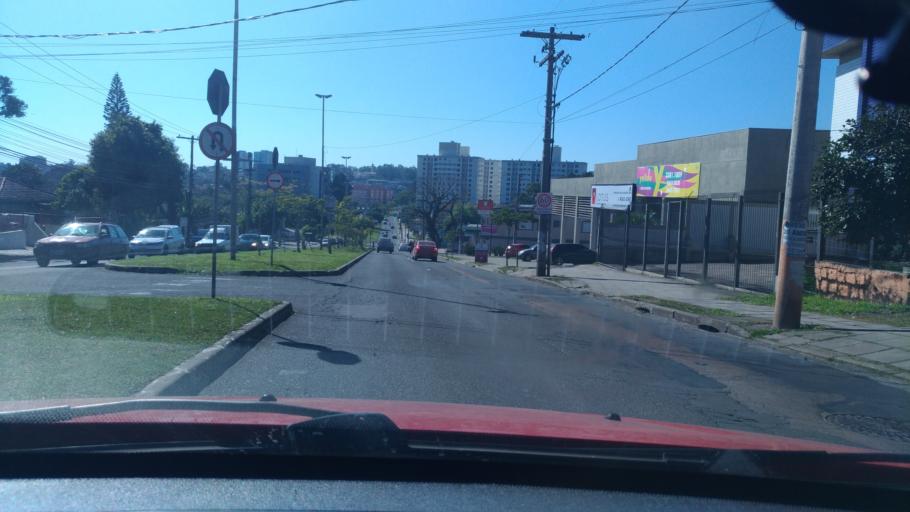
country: BR
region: Rio Grande do Sul
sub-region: Porto Alegre
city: Porto Alegre
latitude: -30.0420
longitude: -51.1337
